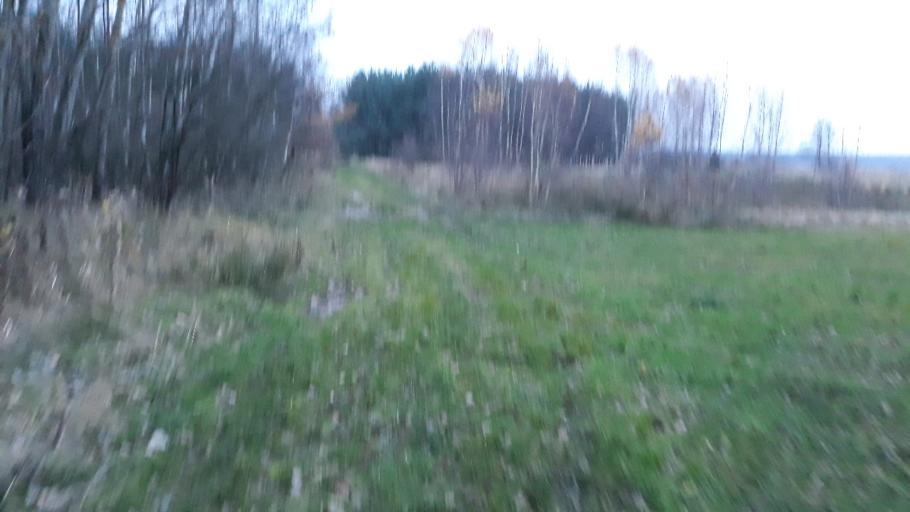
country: PL
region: Lublin Voivodeship
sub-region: Powiat janowski
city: Dzwola
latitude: 50.6658
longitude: 22.5876
